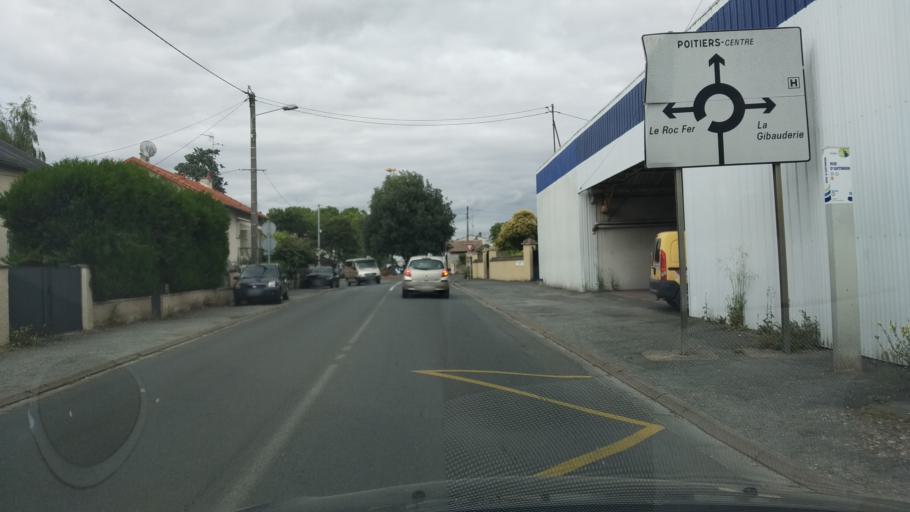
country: FR
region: Poitou-Charentes
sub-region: Departement de la Vienne
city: Saint-Benoit
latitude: 46.5627
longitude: 0.3562
